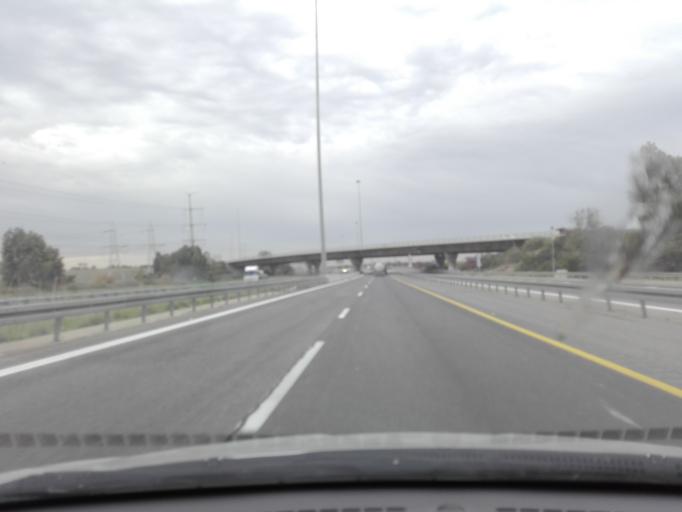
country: IL
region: Central District
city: Ramla
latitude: 31.9078
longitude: 34.8927
